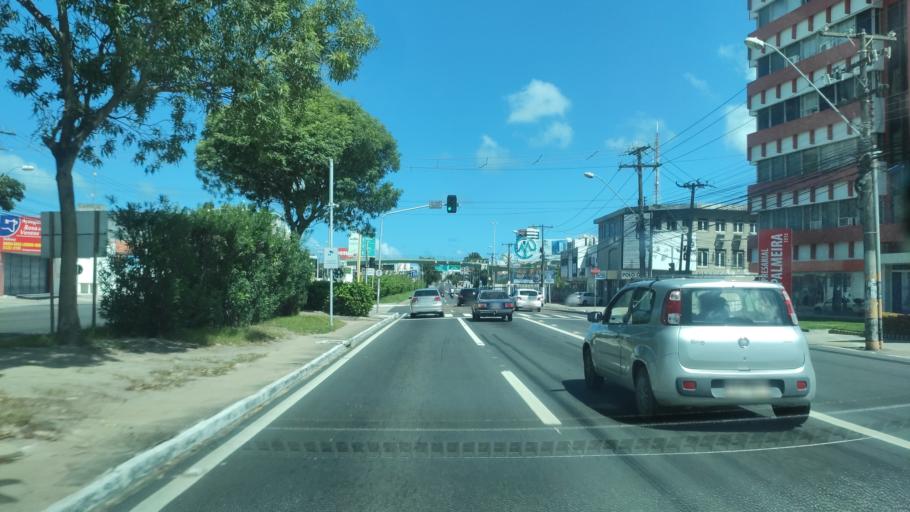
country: BR
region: Alagoas
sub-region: Maceio
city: Maceio
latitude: -9.6369
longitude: -35.7361
